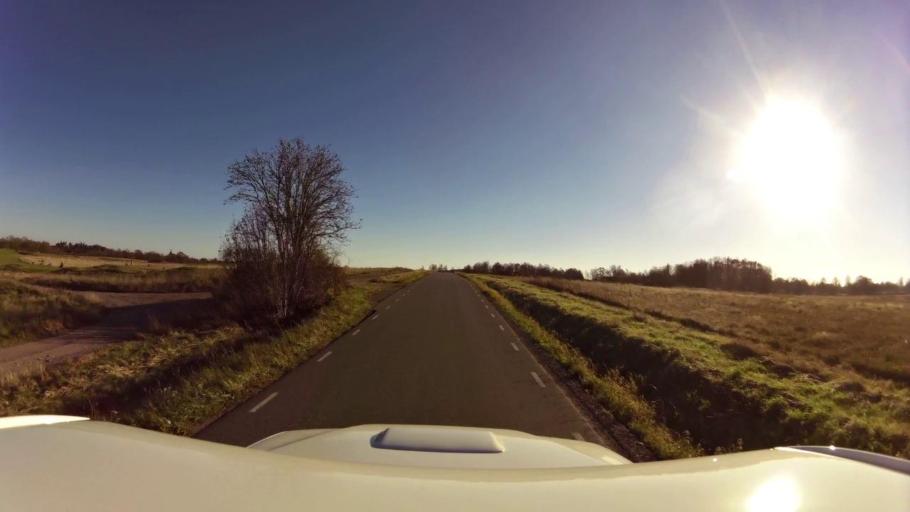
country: SE
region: OEstergoetland
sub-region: Kinda Kommun
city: Rimforsa
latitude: 58.2416
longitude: 15.6719
